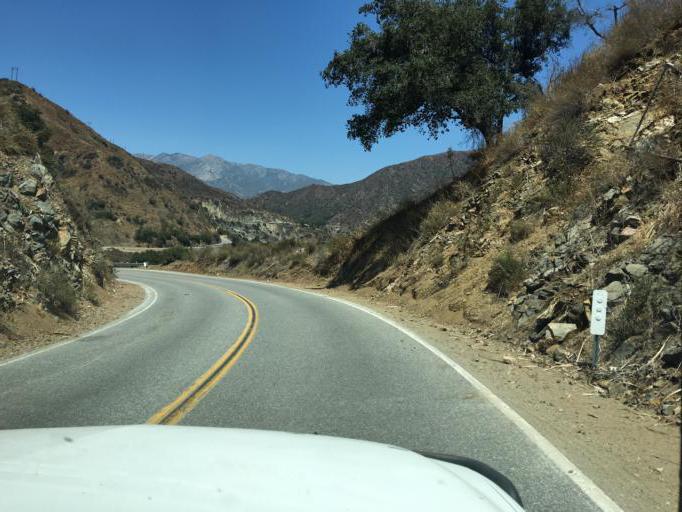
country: US
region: California
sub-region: Los Angeles County
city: Glendora
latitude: 34.1902
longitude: -117.8659
